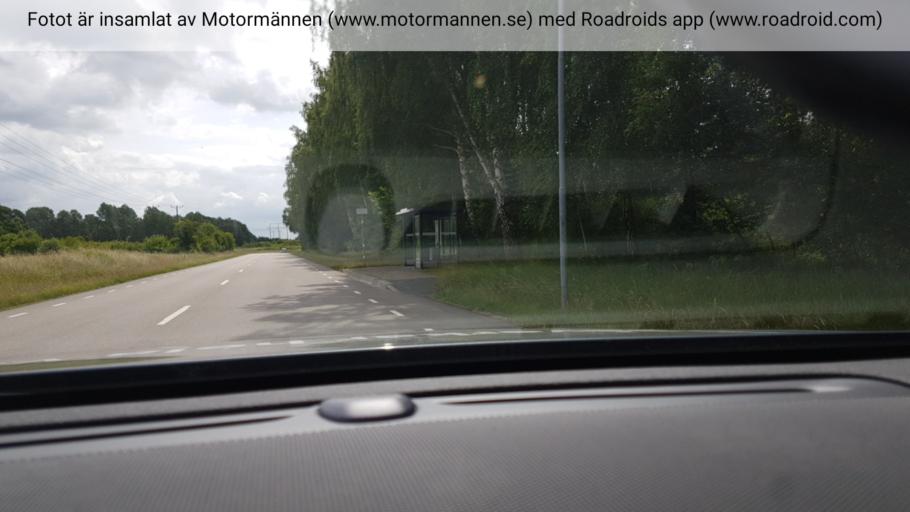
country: SE
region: Skane
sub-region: Hassleholms Kommun
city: Hassleholm
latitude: 56.1742
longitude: 13.7976
